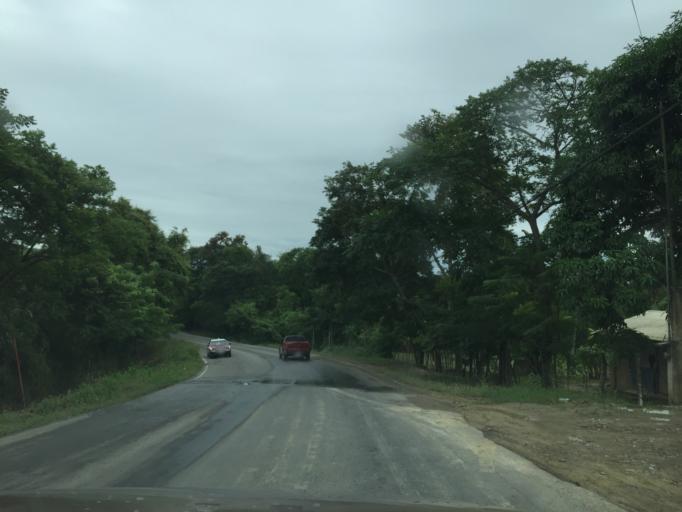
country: MX
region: Veracruz
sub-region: Papantla
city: El Chote
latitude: 20.4377
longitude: -97.3865
